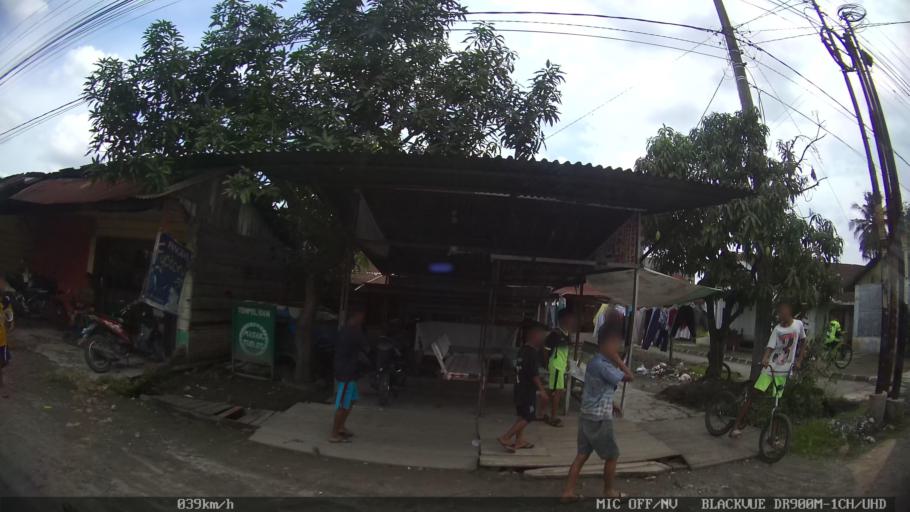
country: ID
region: North Sumatra
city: Medan
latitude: 3.6237
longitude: 98.6614
